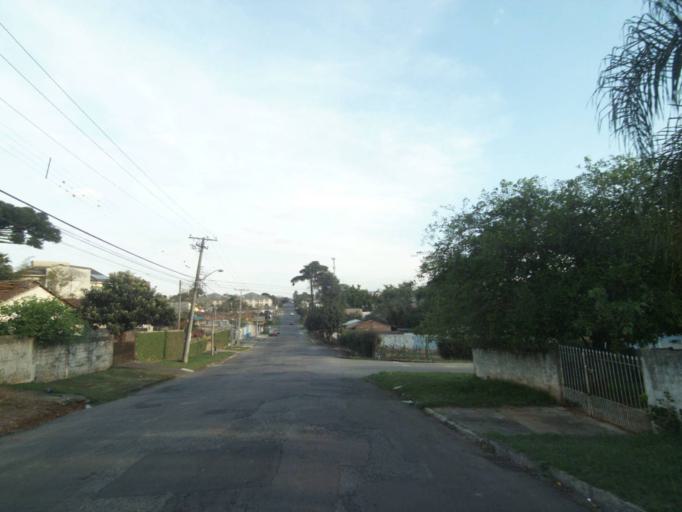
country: BR
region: Parana
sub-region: Curitiba
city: Curitiba
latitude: -25.4655
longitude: -49.3070
